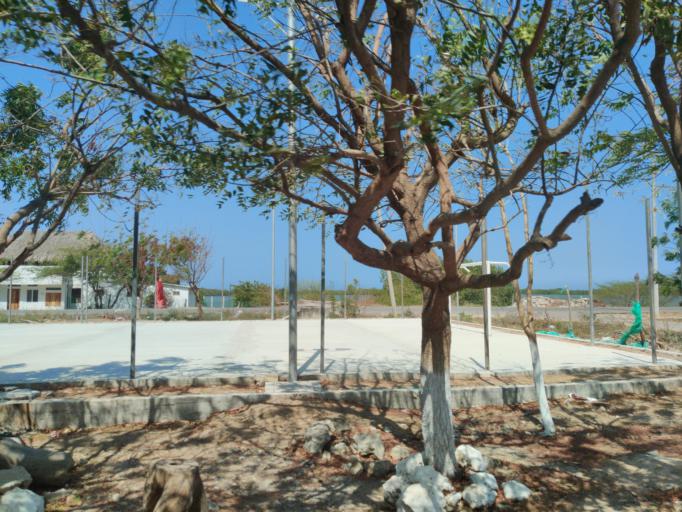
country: CO
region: Bolivar
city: Santa Catalina
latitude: 10.7490
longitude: -75.2629
